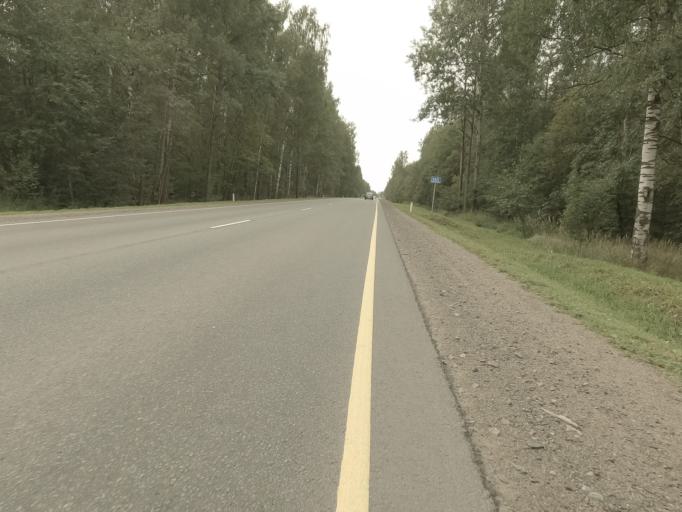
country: RU
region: Leningrad
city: Kirovsk
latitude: 59.8494
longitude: 31.0309
